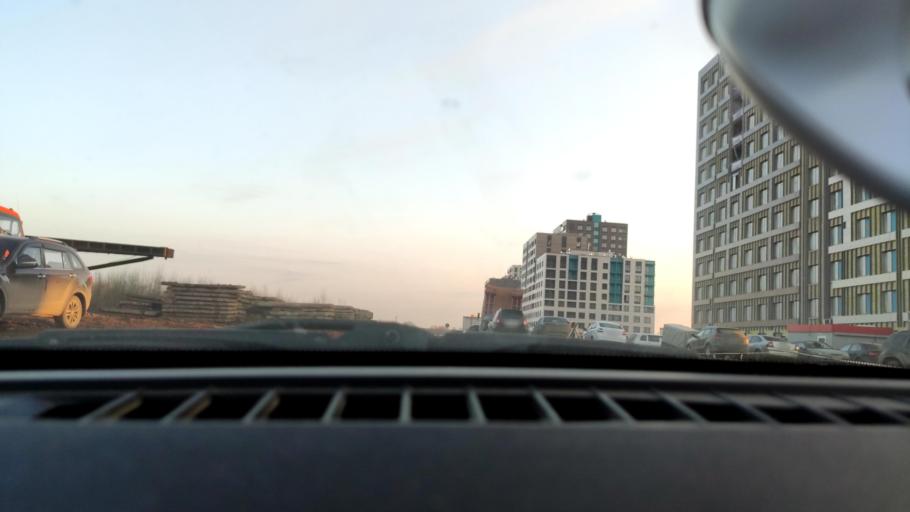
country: RU
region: Perm
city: Perm
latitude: 58.0122
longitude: 56.3308
